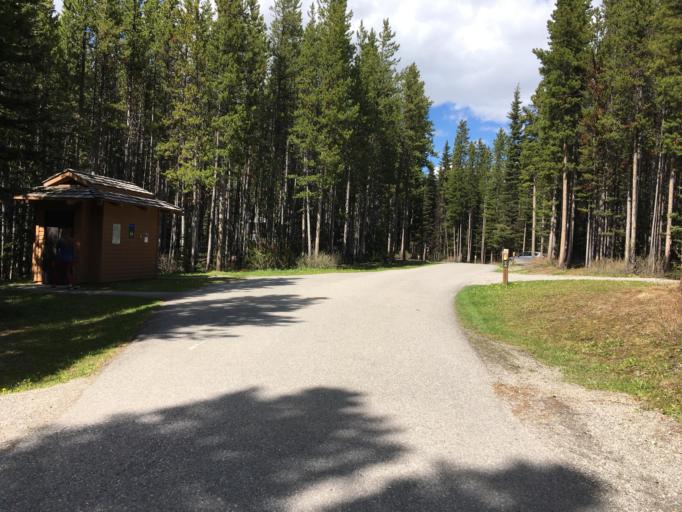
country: CA
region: Alberta
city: Canmore
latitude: 50.6261
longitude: -115.1004
